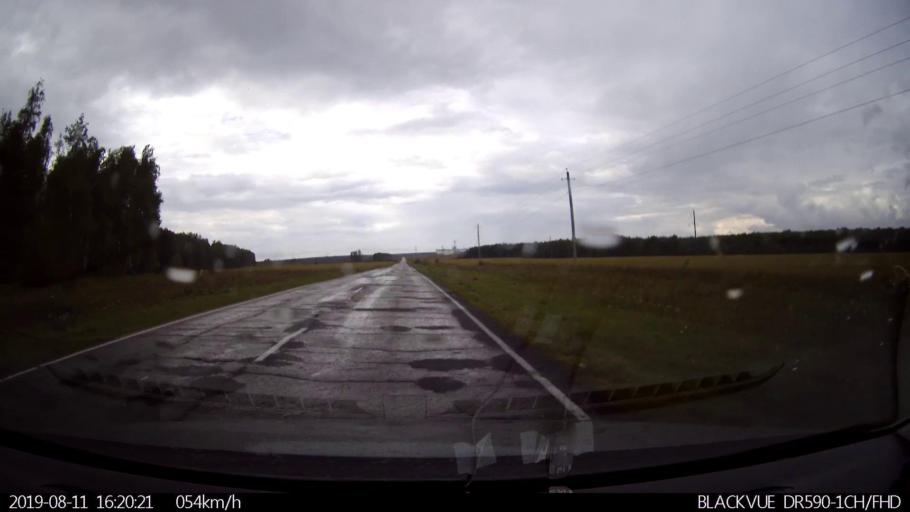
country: RU
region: Ulyanovsk
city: Mayna
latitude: 54.0711
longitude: 47.6034
